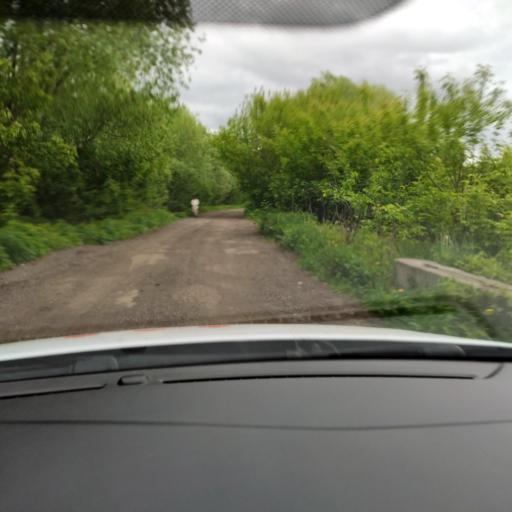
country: RU
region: Tatarstan
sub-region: Gorod Kazan'
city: Kazan
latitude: 55.8103
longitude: 49.2114
